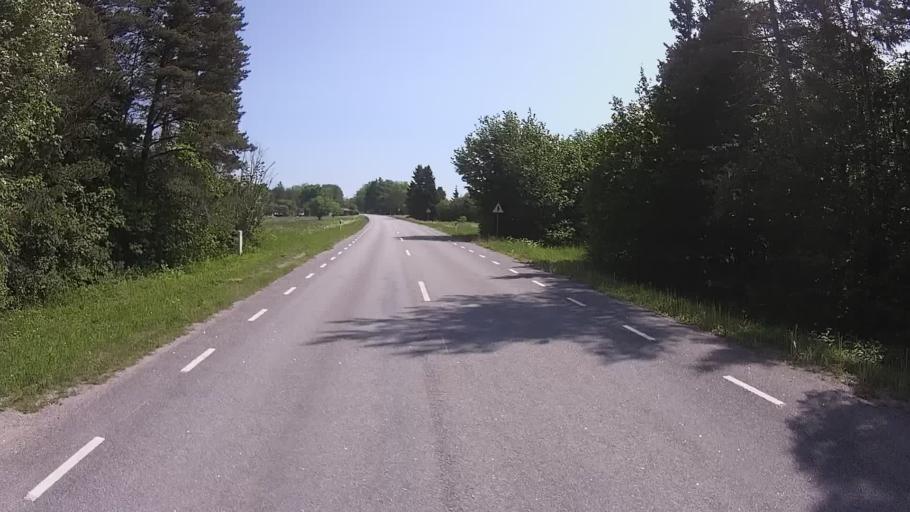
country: EE
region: Saare
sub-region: Kuressaare linn
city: Kuressaare
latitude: 58.3535
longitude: 22.0726
